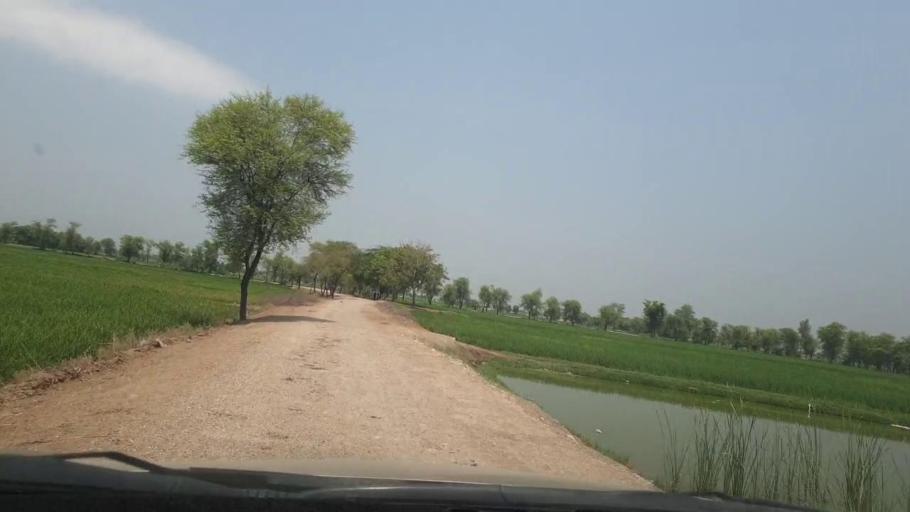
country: PK
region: Sindh
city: Ratodero
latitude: 27.7322
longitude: 68.2967
